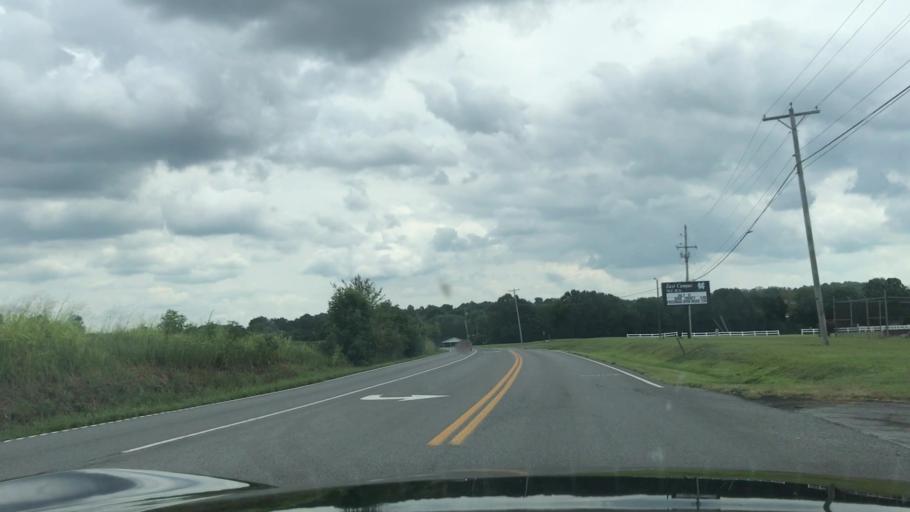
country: US
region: Kentucky
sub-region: Muhlenberg County
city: Greenville
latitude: 37.1983
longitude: -87.1303
